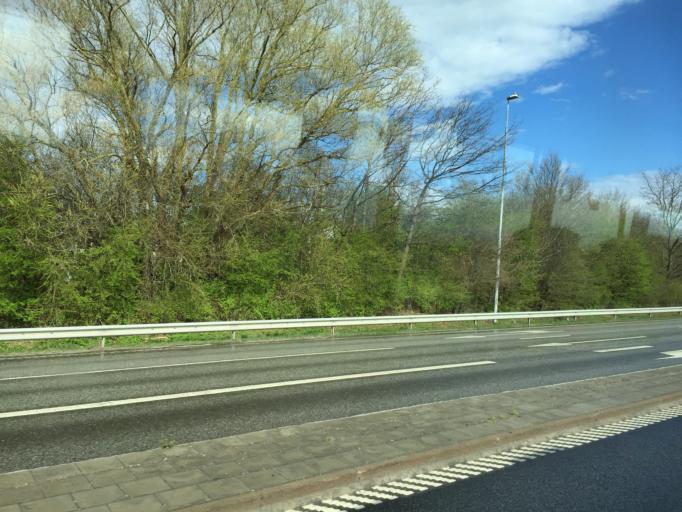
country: SE
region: Skane
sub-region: Lunds Kommun
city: Lund
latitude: 55.6922
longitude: 13.2412
